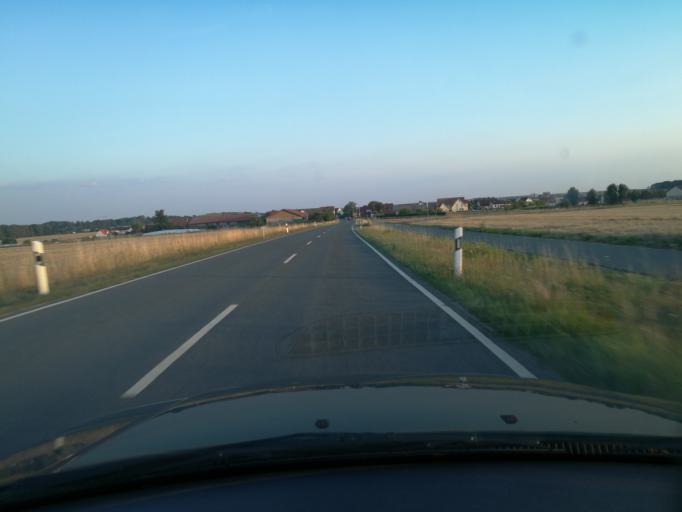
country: DE
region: Bavaria
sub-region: Regierungsbezirk Mittelfranken
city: Herzogenaurach
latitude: 49.5970
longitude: 10.8956
